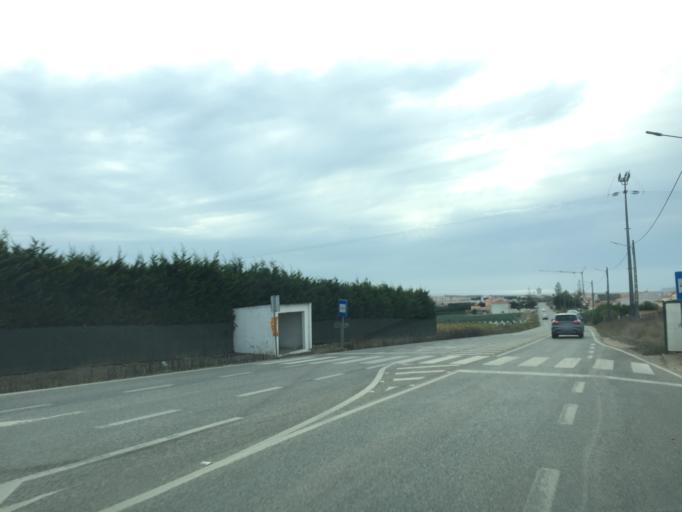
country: PT
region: Leiria
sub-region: Peniche
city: Atouguia da Baleia
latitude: 39.3354
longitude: -9.2995
